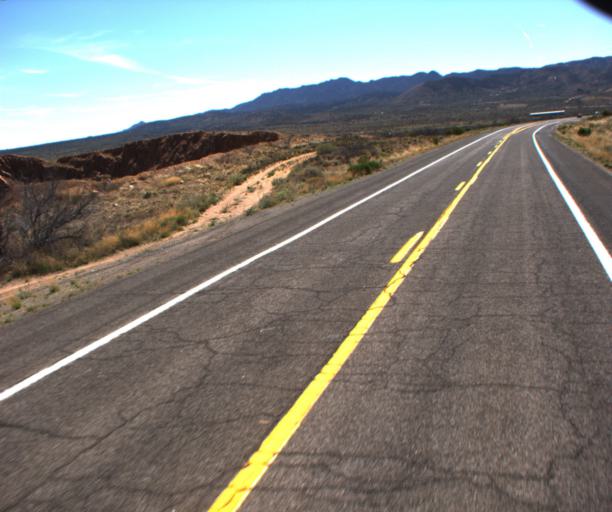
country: US
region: Arizona
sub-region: Mohave County
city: Peach Springs
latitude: 35.3627
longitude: -113.6863
